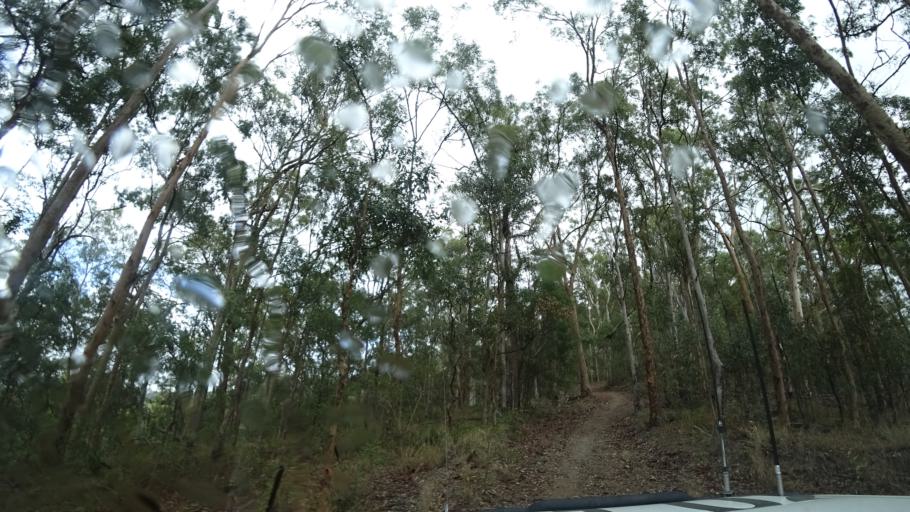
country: AU
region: Queensland
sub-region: Brisbane
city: Pullenvale
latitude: -27.4584
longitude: 152.8439
